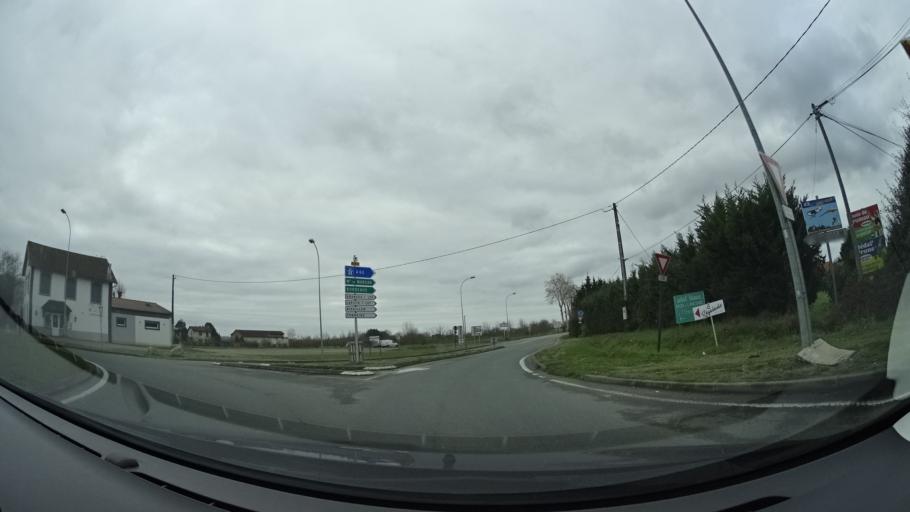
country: FR
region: Aquitaine
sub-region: Departement du Lot-et-Garonne
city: Castelmoron-sur-Lot
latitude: 44.3781
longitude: 0.5020
